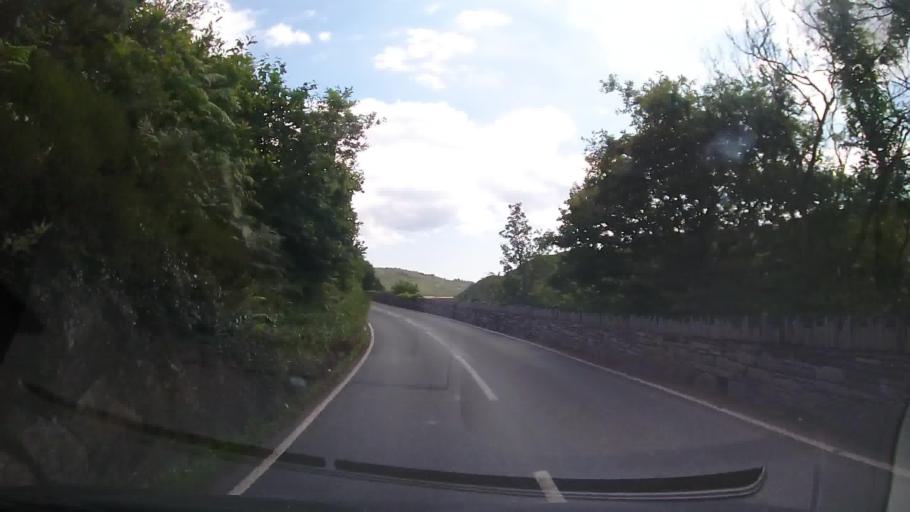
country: GB
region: Wales
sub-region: Gwynedd
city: Penrhyndeudraeth
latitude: 52.9340
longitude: -4.0401
